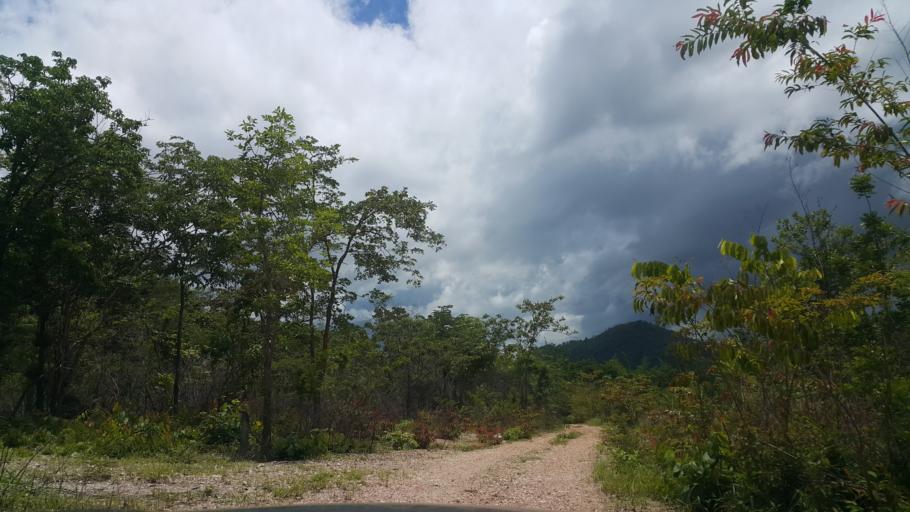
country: TH
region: Sukhothai
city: Thung Saliam
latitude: 17.3321
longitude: 99.4697
